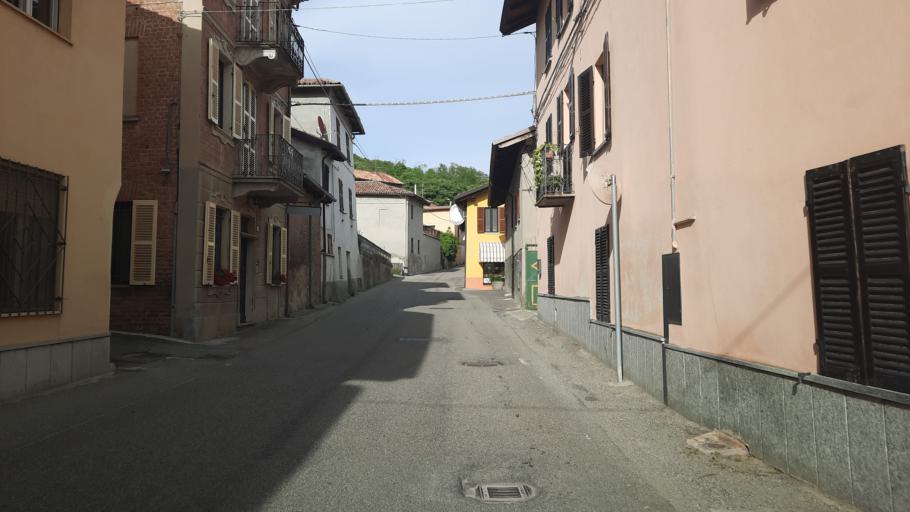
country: IT
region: Piedmont
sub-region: Provincia di Alessandria
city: Alfiano Natta
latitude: 45.0478
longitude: 8.2092
